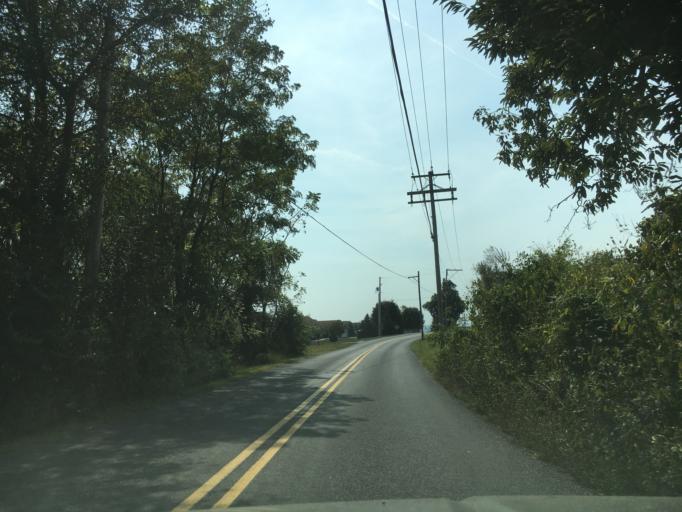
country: US
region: Pennsylvania
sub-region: Berks County
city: Topton
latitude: 40.5652
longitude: -75.7055
